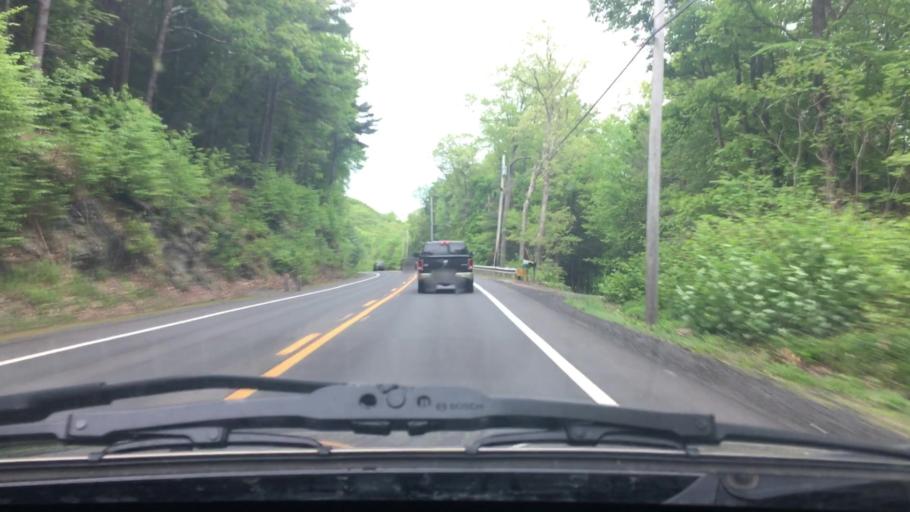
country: US
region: Massachusetts
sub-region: Franklin County
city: Leverett
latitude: 42.4700
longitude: -72.5146
